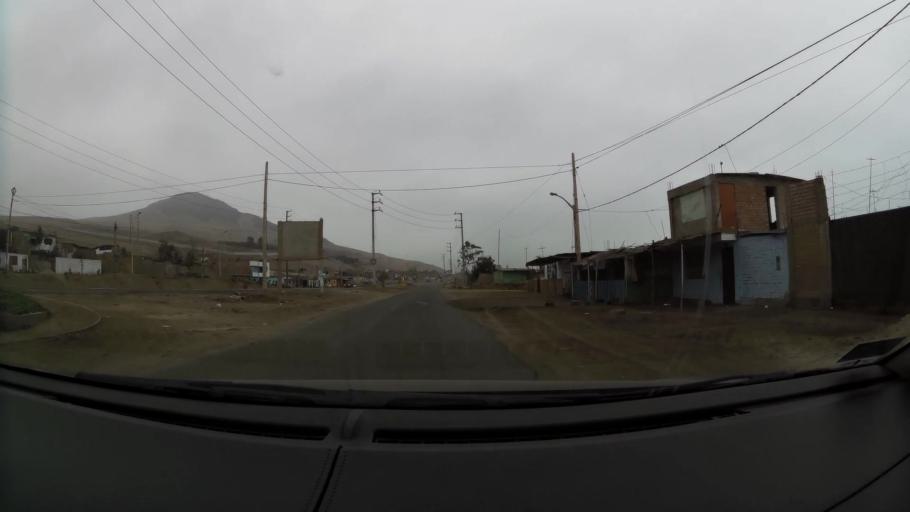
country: PE
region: Lima
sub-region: Provincia de Huaral
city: Chancay
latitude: -11.5973
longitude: -77.2533
